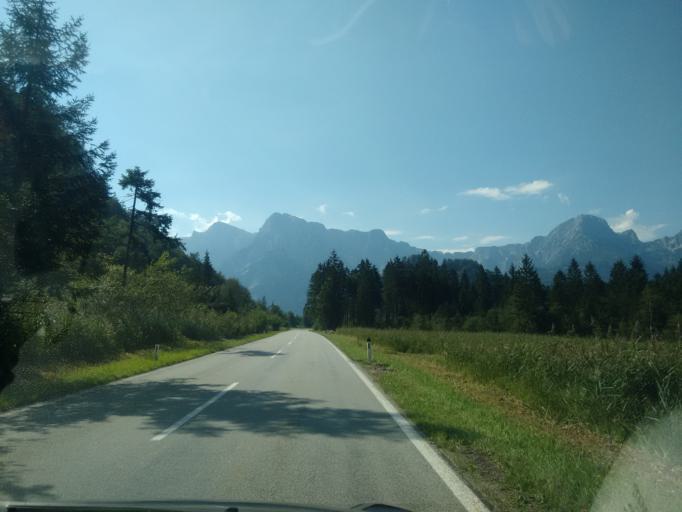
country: AT
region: Upper Austria
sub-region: Politischer Bezirk Gmunden
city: Gruenau im Almtal
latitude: 47.7712
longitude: 13.9570
